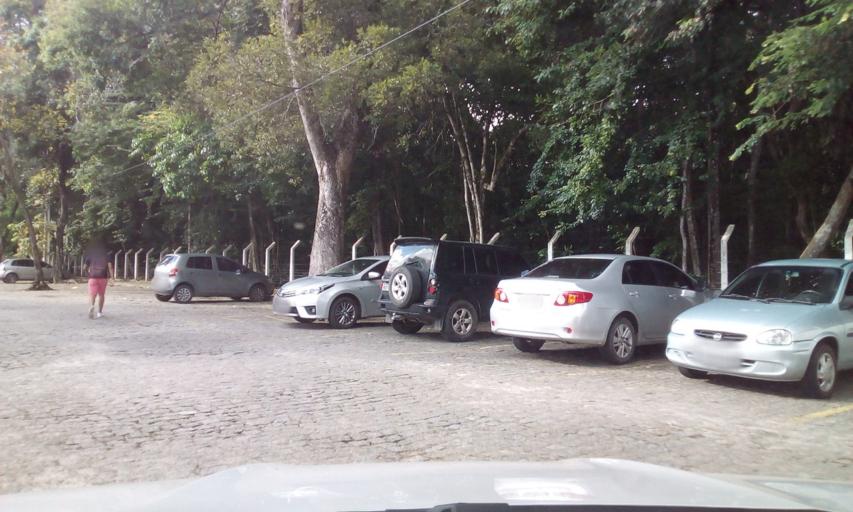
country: BR
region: Paraiba
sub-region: Joao Pessoa
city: Joao Pessoa
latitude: -7.1398
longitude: -34.8492
